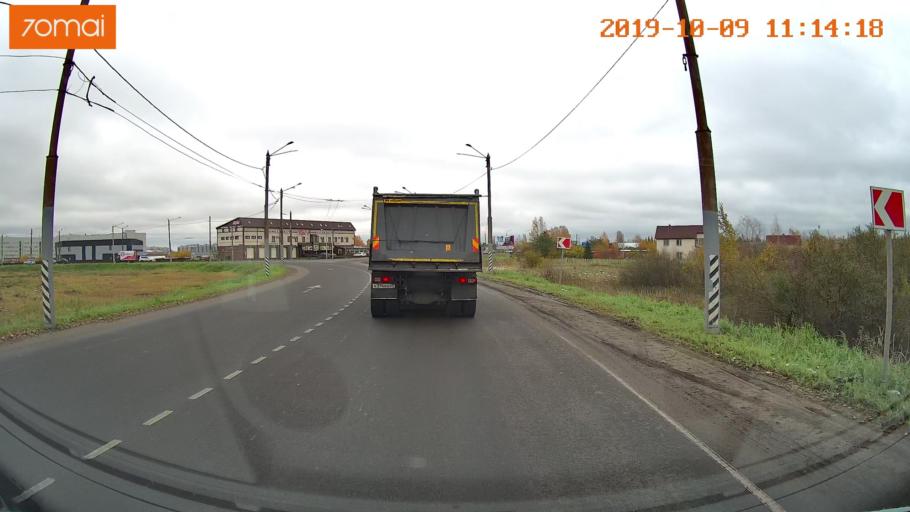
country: RU
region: Vologda
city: Vologda
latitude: 59.1865
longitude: 39.8516
